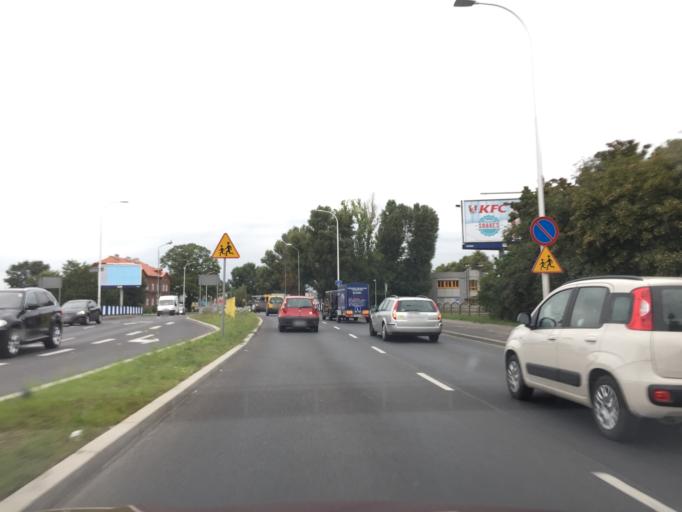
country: PL
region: Greater Poland Voivodeship
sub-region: Kalisz
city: Kalisz
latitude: 51.7625
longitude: 18.0786
